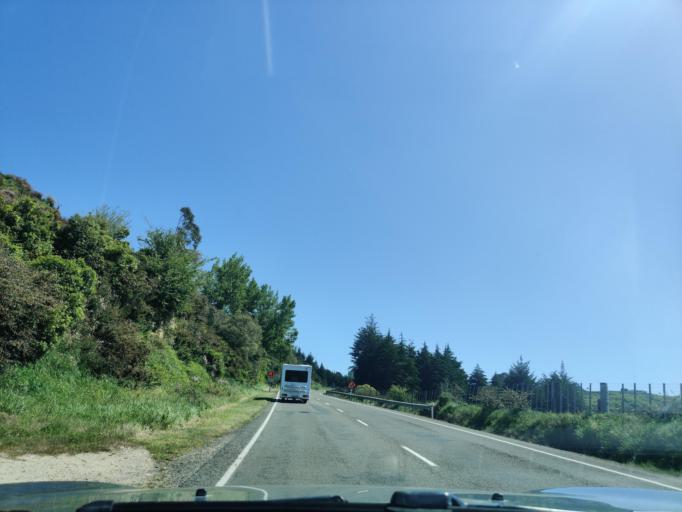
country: NZ
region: Manawatu-Wanganui
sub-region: Wanganui District
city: Wanganui
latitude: -39.8454
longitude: 174.9259
